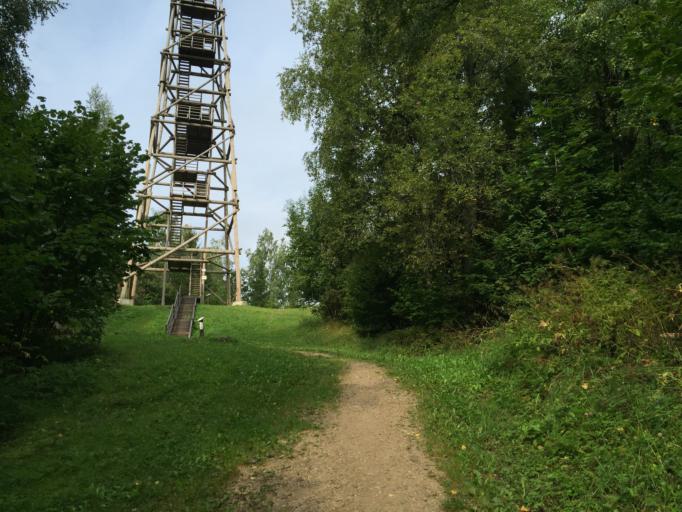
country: LV
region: Dagda
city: Dagda
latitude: 56.2708
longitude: 27.6553
